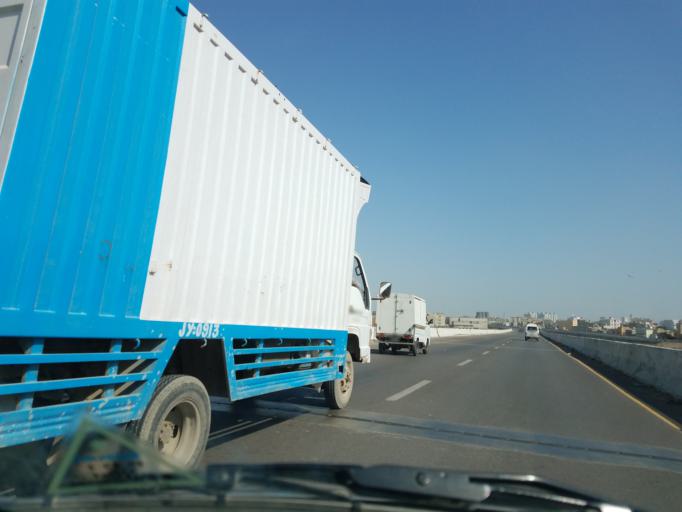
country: PK
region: Sindh
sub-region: Karachi District
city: Karachi
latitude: 24.8817
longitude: 67.0061
